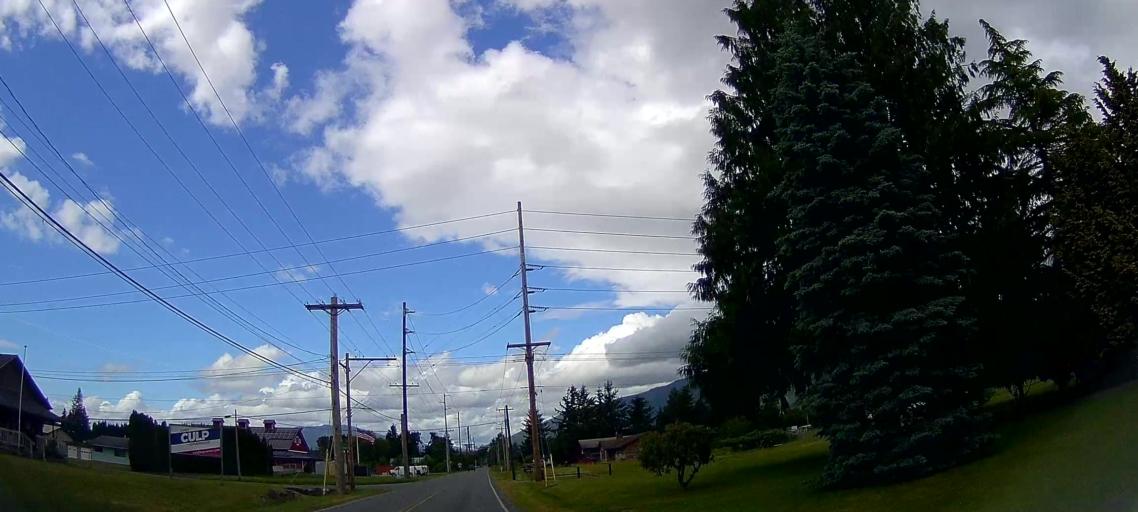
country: US
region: Washington
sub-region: Skagit County
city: Sedro-Woolley
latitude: 48.5064
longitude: -122.2100
